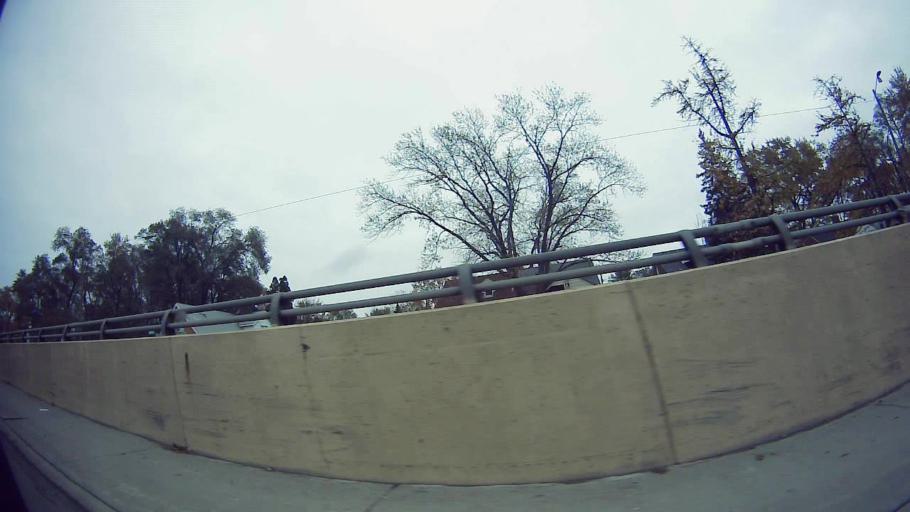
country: US
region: Michigan
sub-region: Oakland County
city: Oak Park
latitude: 42.3954
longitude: -83.2179
